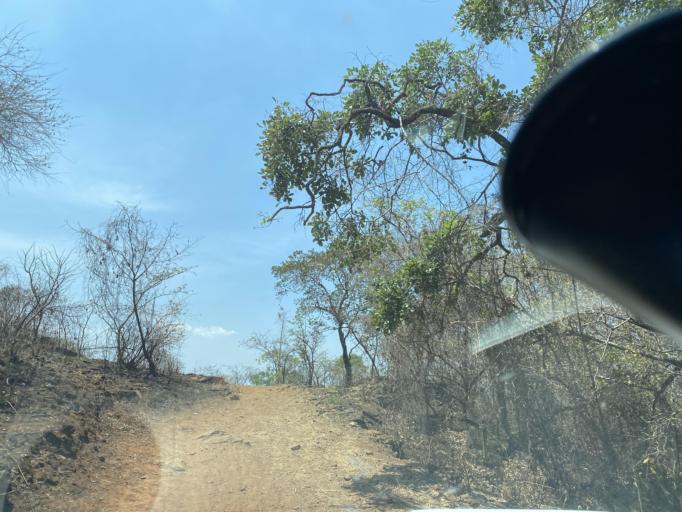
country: ZM
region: Lusaka
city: Kafue
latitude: -15.8035
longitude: 28.4493
